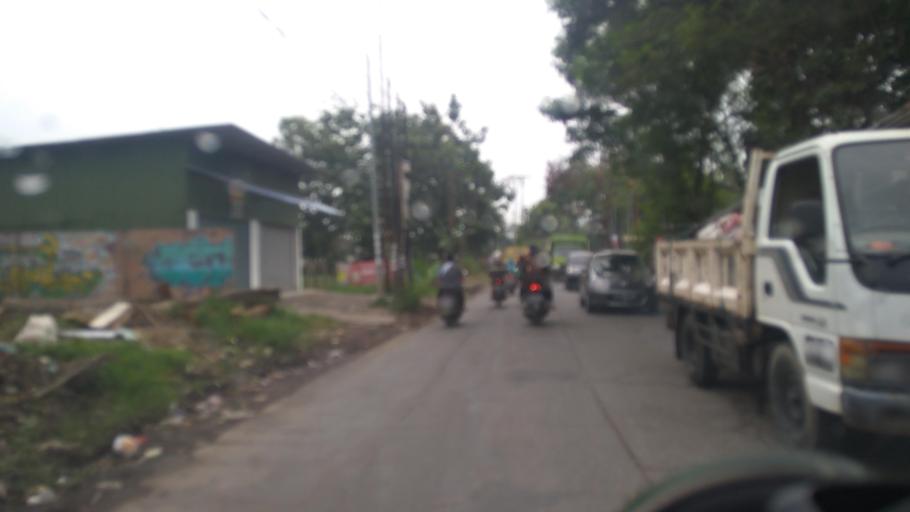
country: ID
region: West Java
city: Bekasi
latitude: -6.2055
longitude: 107.0320
